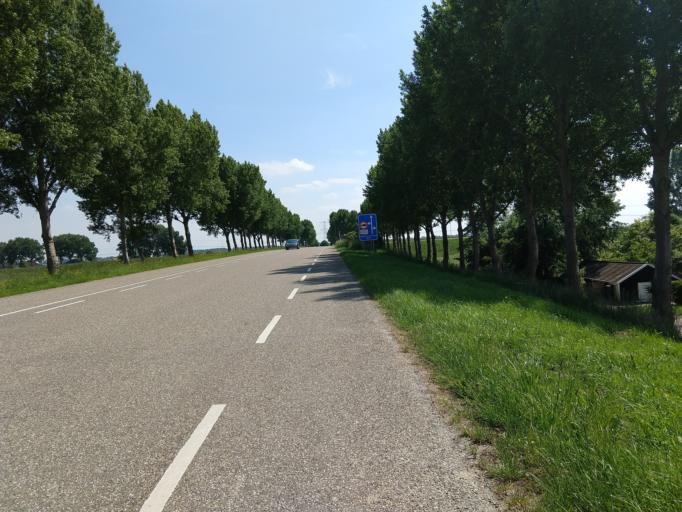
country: NL
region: Zeeland
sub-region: Gemeente Borsele
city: Borssele
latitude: 51.4434
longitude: 3.7682
